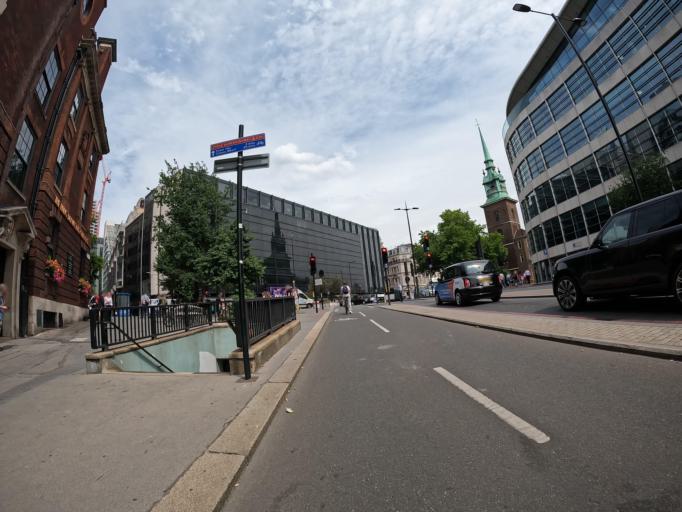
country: GB
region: England
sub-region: Greater London
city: Brixton Hill
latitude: 51.4654
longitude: -0.1255
